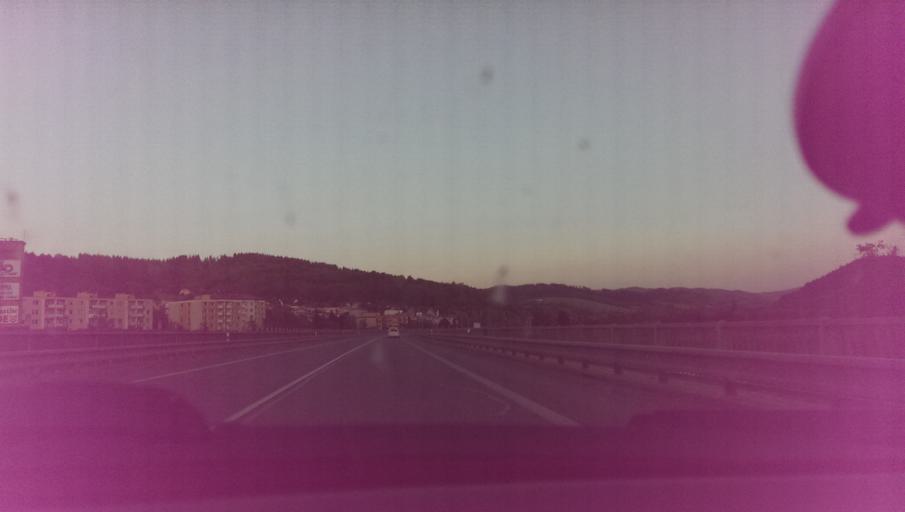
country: CZ
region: Zlin
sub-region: Okres Vsetin
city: Vsetin
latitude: 49.3290
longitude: 17.9995
